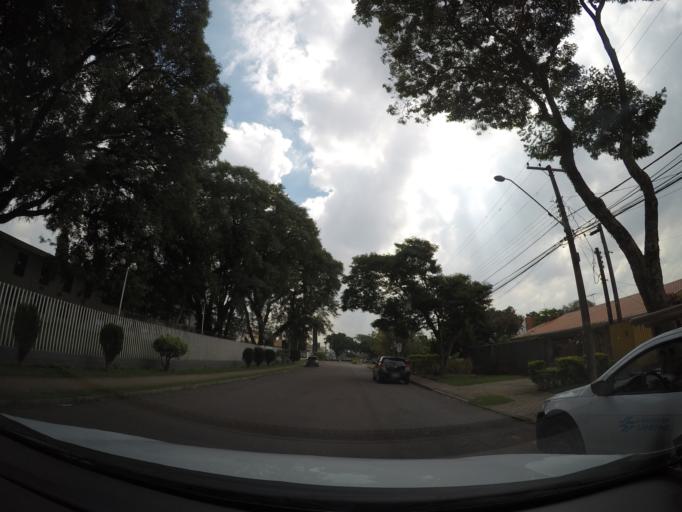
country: BR
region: Parana
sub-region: Curitiba
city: Curitiba
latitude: -25.4837
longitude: -49.2559
